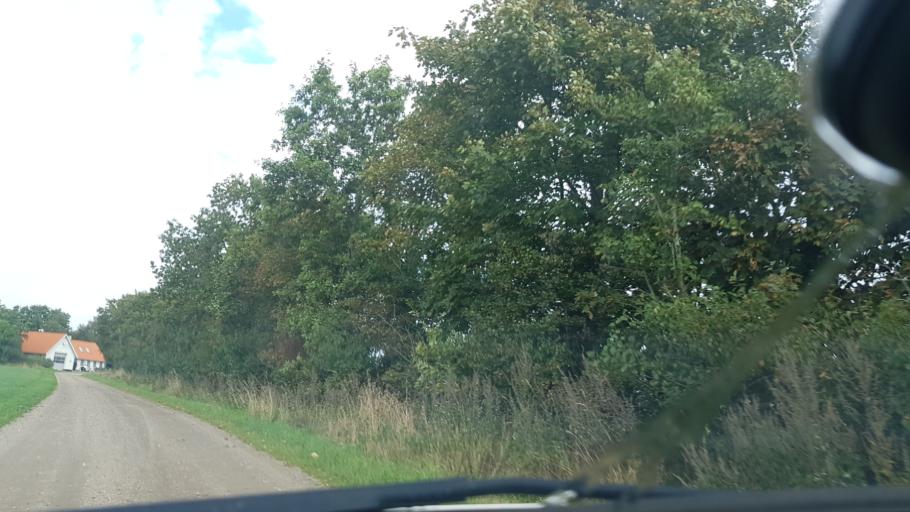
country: DK
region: South Denmark
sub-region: Vejen Kommune
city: Holsted
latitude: 55.4428
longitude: 8.9266
